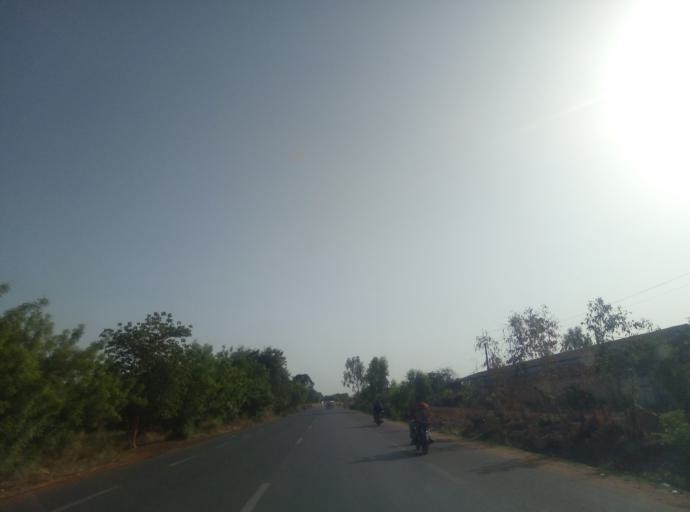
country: ML
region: Bamako
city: Bamako
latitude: 12.5836
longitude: -7.7722
